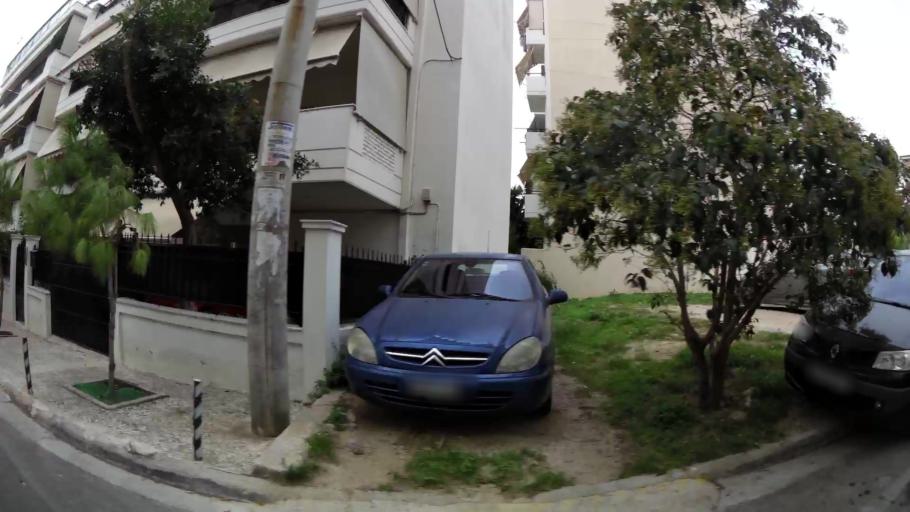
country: GR
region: Attica
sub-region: Nomarchia Athinas
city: Alimos
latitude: 37.9148
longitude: 23.7240
